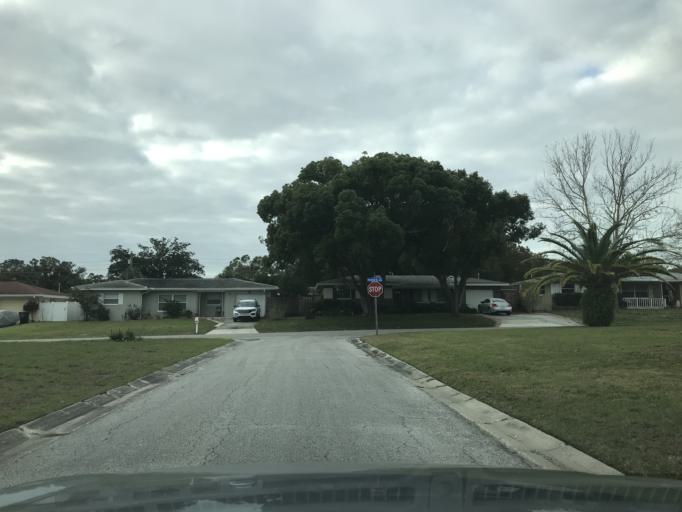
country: US
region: Florida
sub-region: Pinellas County
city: Belleair
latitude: 27.9401
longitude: -82.7825
